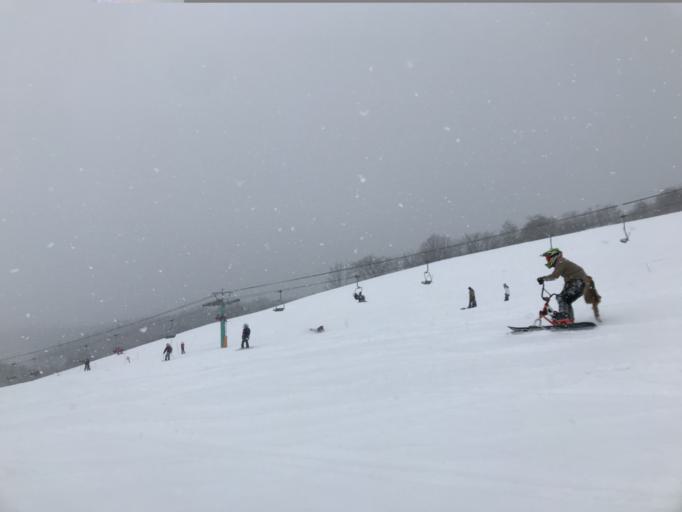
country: JP
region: Nagano
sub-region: Kitaazumi Gun
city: Hakuba
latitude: 36.7502
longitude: 137.8565
